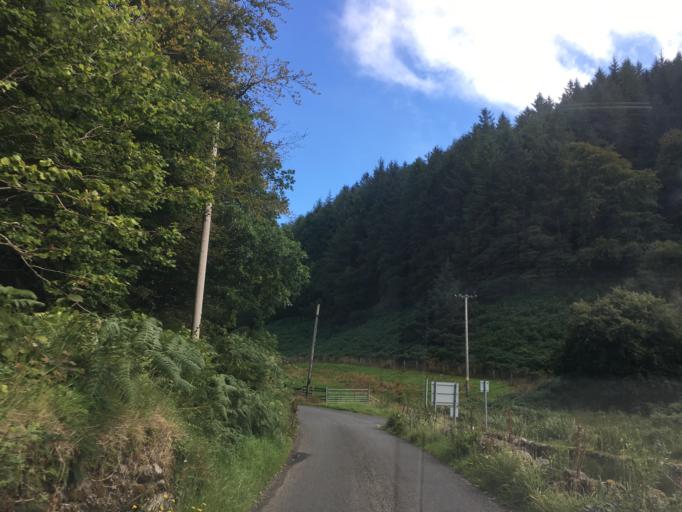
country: GB
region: Scotland
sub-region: Argyll and Bute
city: Ardrishaig
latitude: 56.0856
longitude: -5.5600
